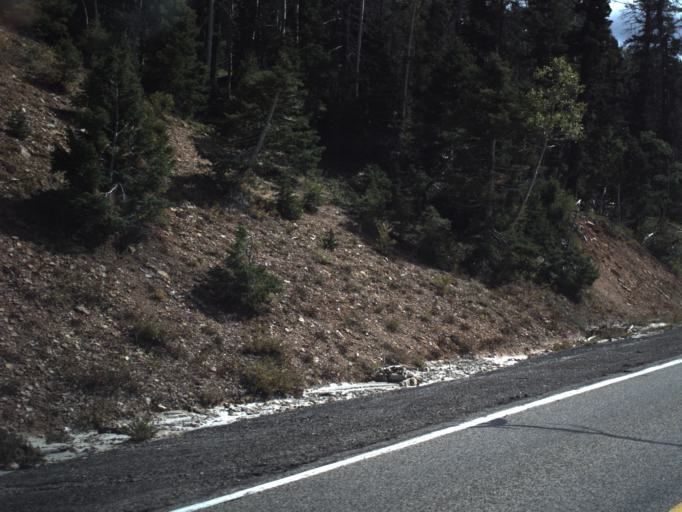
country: US
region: Utah
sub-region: Iron County
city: Cedar City
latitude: 37.5857
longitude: -112.8837
